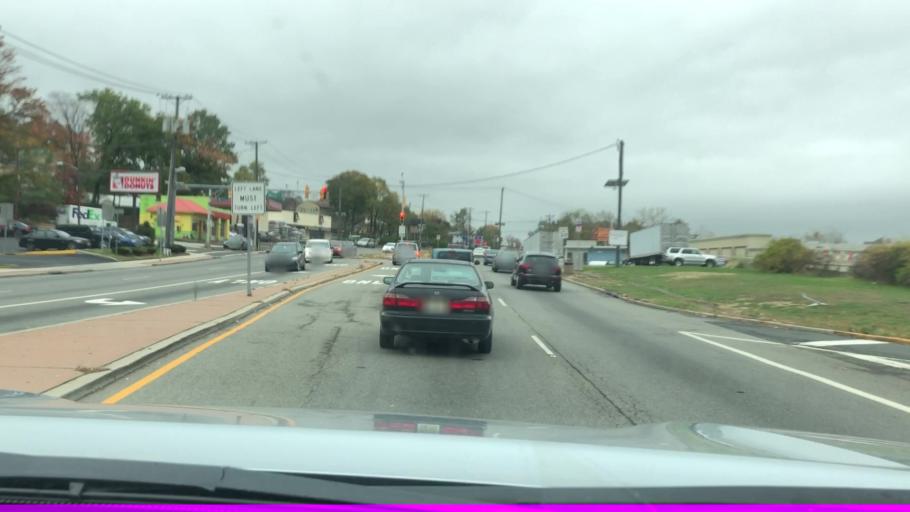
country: US
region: New Jersey
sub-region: Bergen County
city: Ridgefield
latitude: 40.8327
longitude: -74.0103
